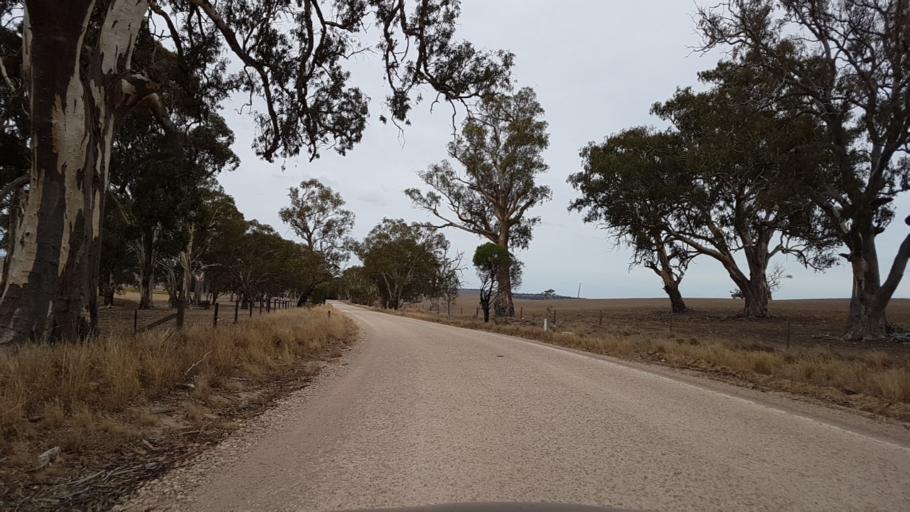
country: AU
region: South Australia
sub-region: Adelaide Hills
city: Birdwood
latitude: -34.9338
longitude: 139.0714
